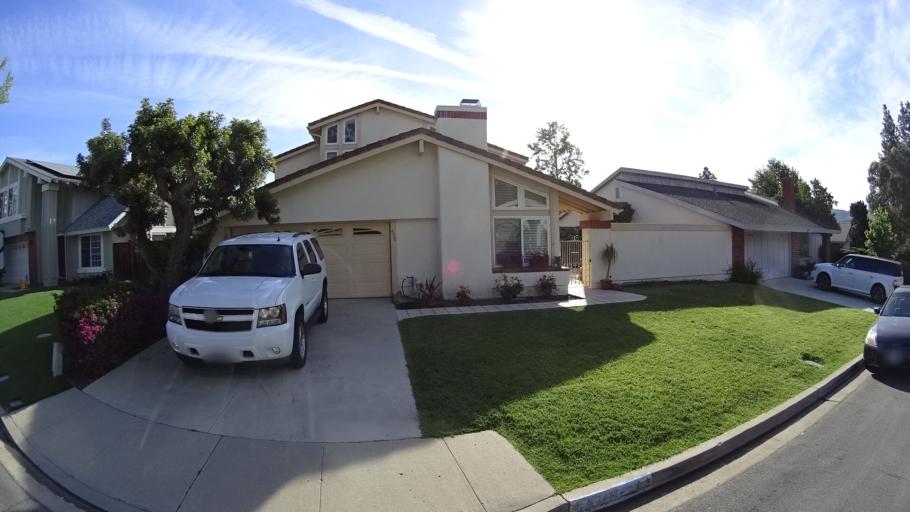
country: US
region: California
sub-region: Ventura County
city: Casa Conejo
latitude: 34.1829
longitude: -118.9558
